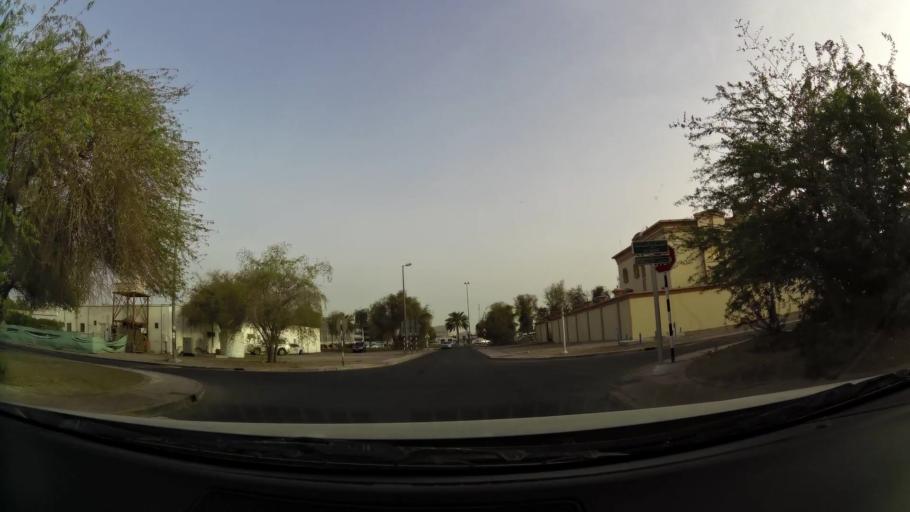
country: AE
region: Abu Dhabi
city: Al Ain
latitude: 24.2428
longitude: 55.7330
